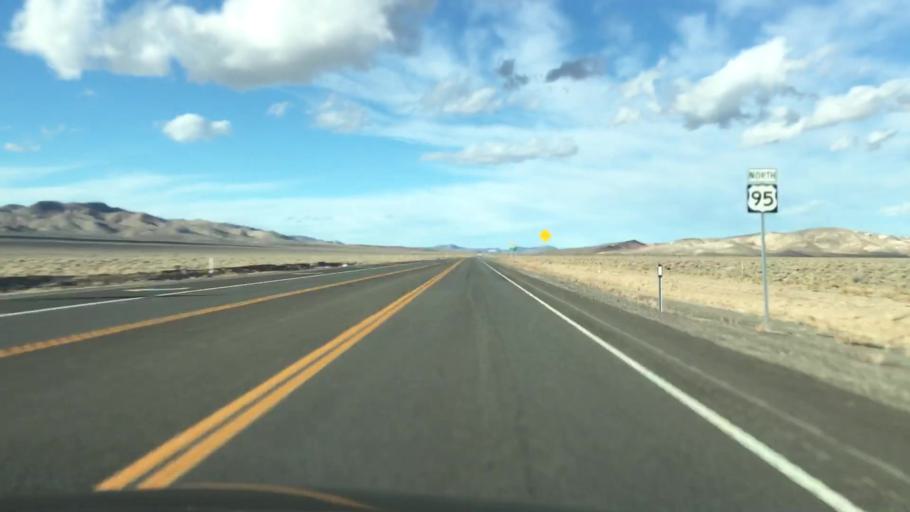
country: US
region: Nevada
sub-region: Esmeralda County
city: Goldfield
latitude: 37.5029
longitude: -117.1848
